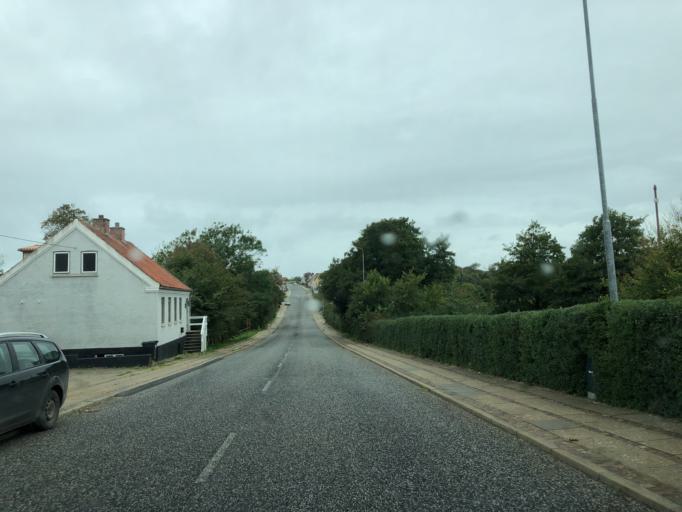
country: DK
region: North Denmark
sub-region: Thisted Kommune
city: Hurup
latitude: 56.7125
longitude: 8.4020
